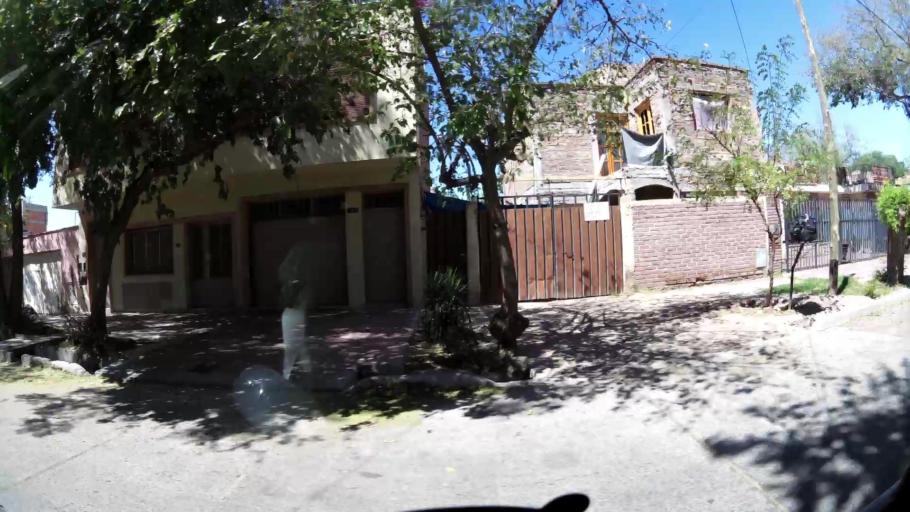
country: AR
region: Mendoza
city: Las Heras
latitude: -32.8610
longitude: -68.8463
